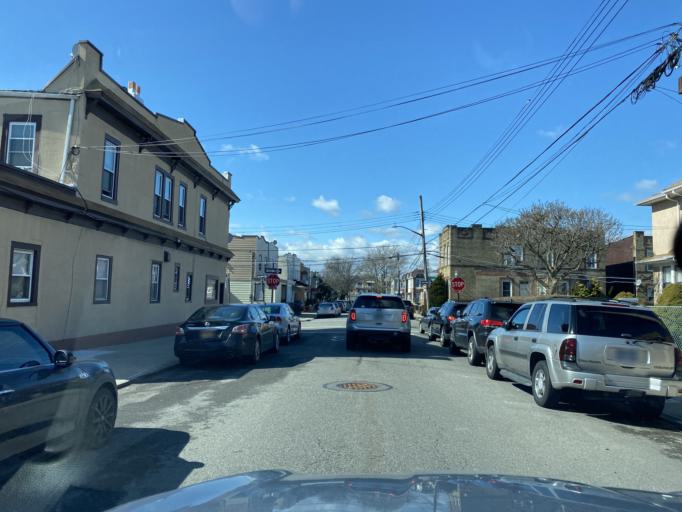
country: US
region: New York
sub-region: Kings County
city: East New York
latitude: 40.7122
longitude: -73.8771
